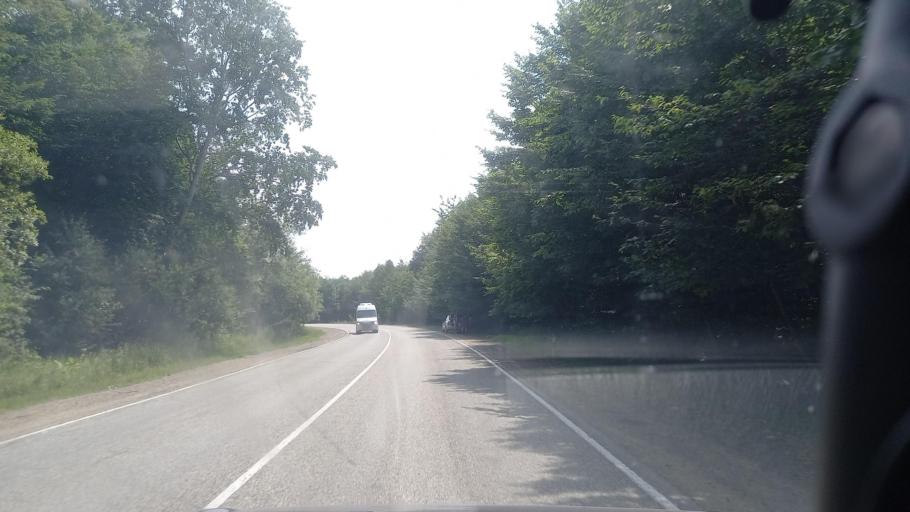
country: RU
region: Karachayevo-Cherkesiya
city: Kurdzhinovo
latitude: 44.0387
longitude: 40.9084
